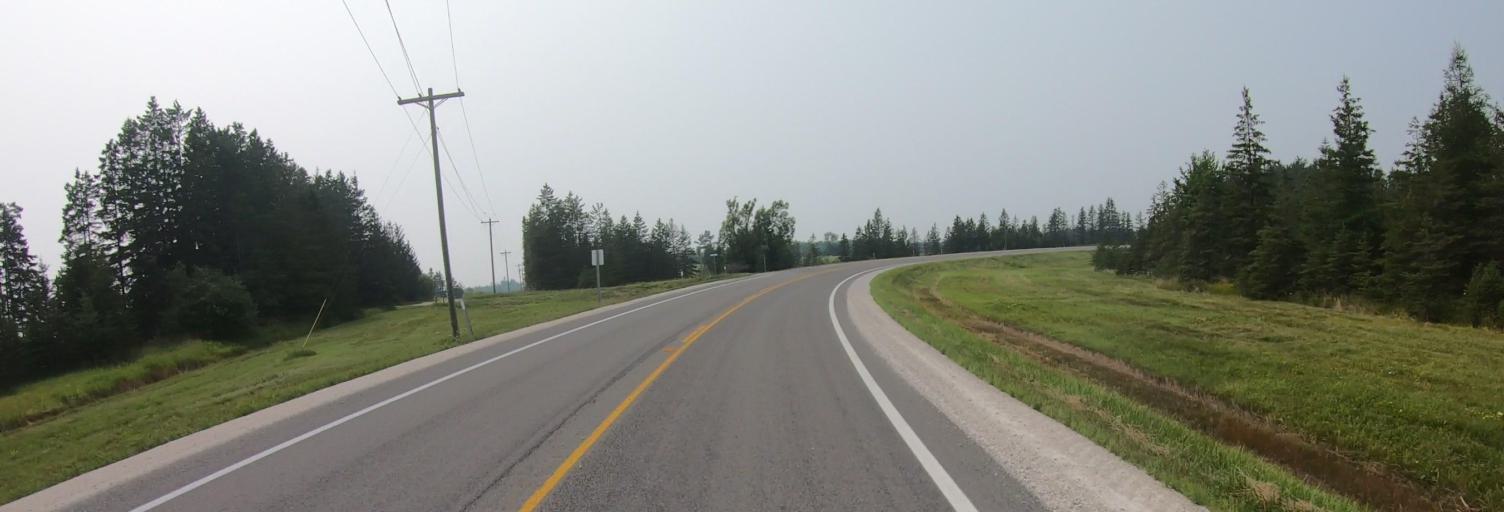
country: US
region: Michigan
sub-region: Chippewa County
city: Sault Ste. Marie
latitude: 46.0717
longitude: -84.2371
